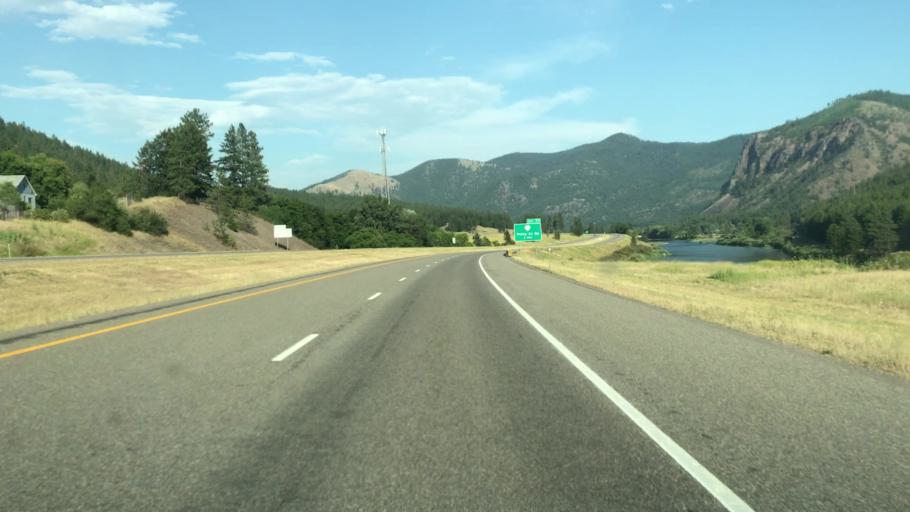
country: US
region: Montana
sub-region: Missoula County
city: Frenchtown
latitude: 47.0004
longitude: -114.4726
